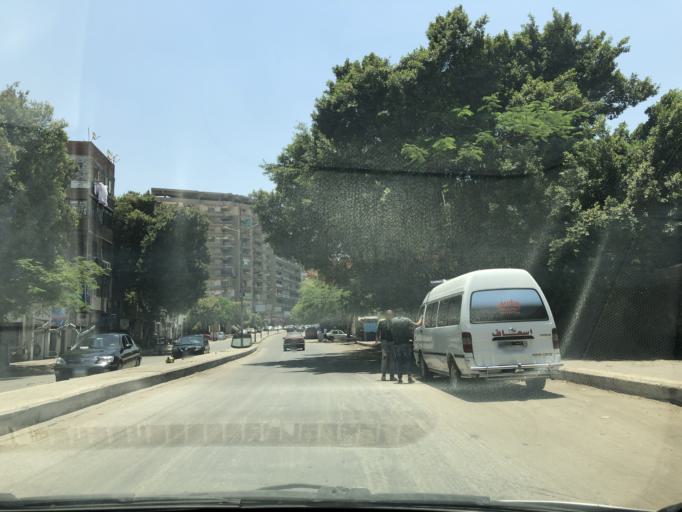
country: EG
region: Muhafazat al Qahirah
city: Cairo
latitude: 30.0663
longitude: 31.2713
